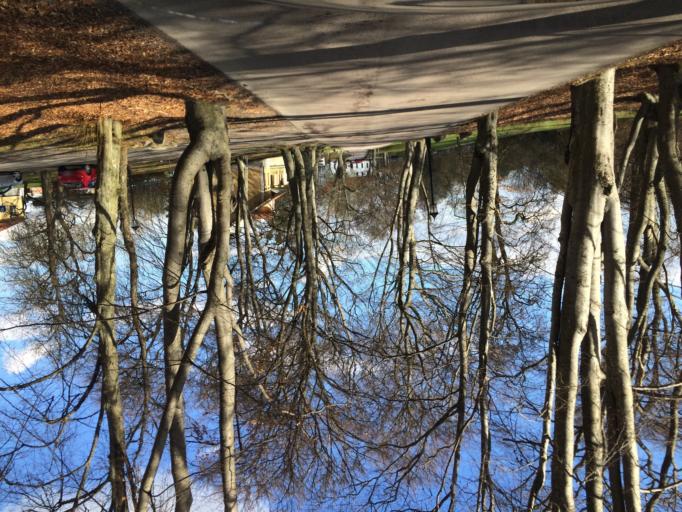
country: SE
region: Soedermanland
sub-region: Eskilstuna Kommun
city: Eskilstuna
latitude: 59.4451
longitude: 16.6230
